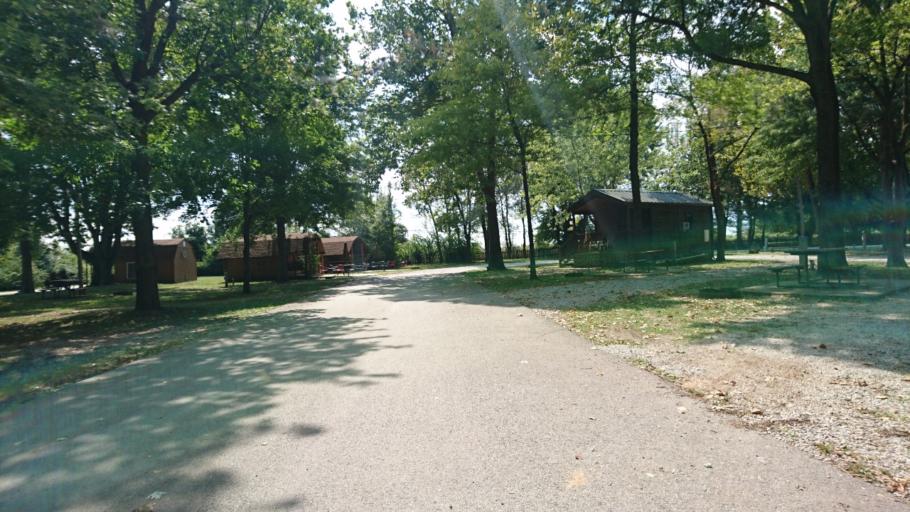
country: US
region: Missouri
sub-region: Greene County
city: Battlefield
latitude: 37.1989
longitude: -93.4028
